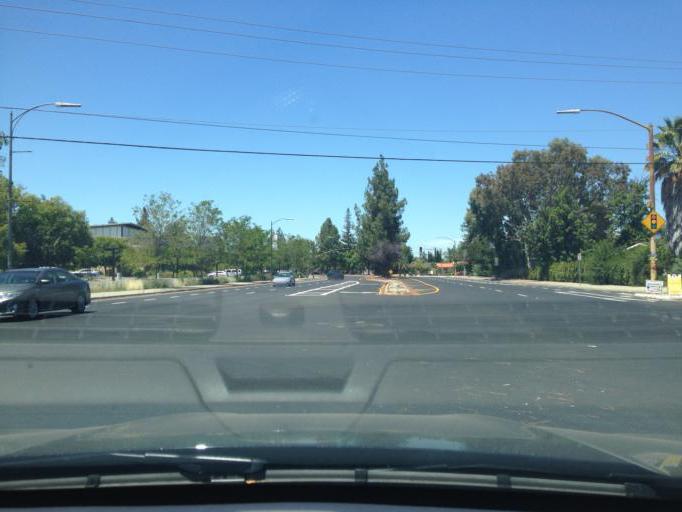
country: US
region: California
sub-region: Santa Clara County
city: Seven Trees
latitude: 37.2213
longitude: -121.8671
